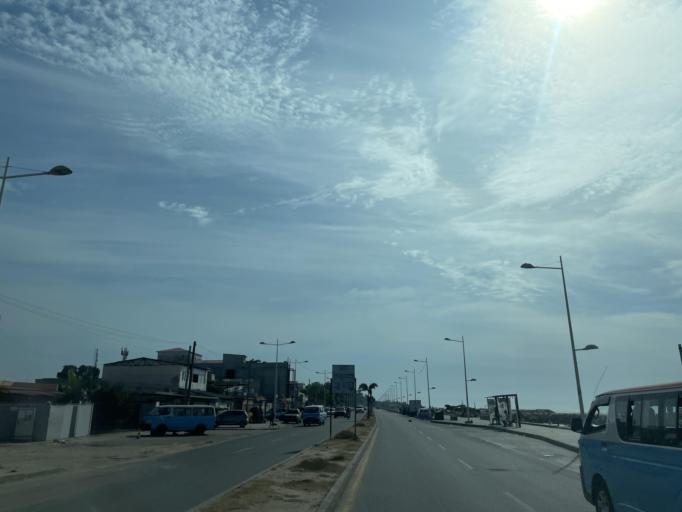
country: AO
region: Luanda
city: Luanda
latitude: -8.7719
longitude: 13.2502
